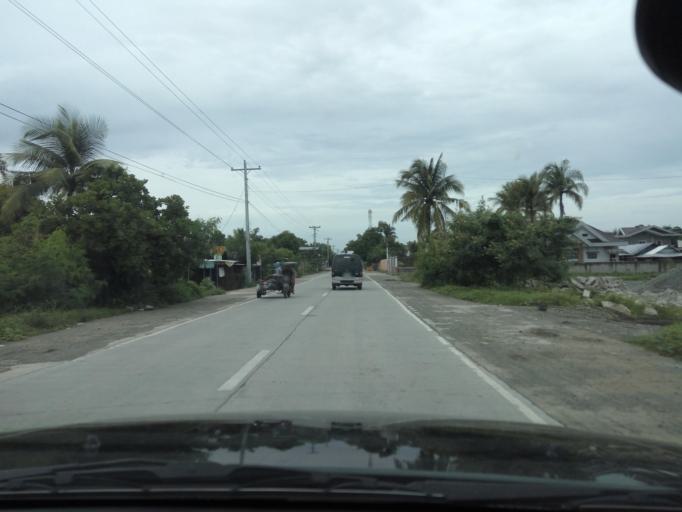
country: PH
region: Central Luzon
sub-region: Province of Nueva Ecija
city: Rajal Norte
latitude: 15.4430
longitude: 120.8464
